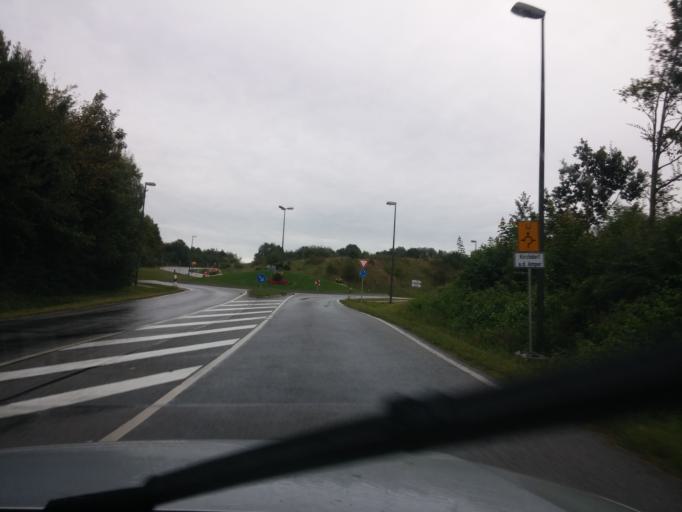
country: DE
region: Bavaria
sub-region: Upper Bavaria
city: Reichertshausen
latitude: 48.4640
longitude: 11.5099
